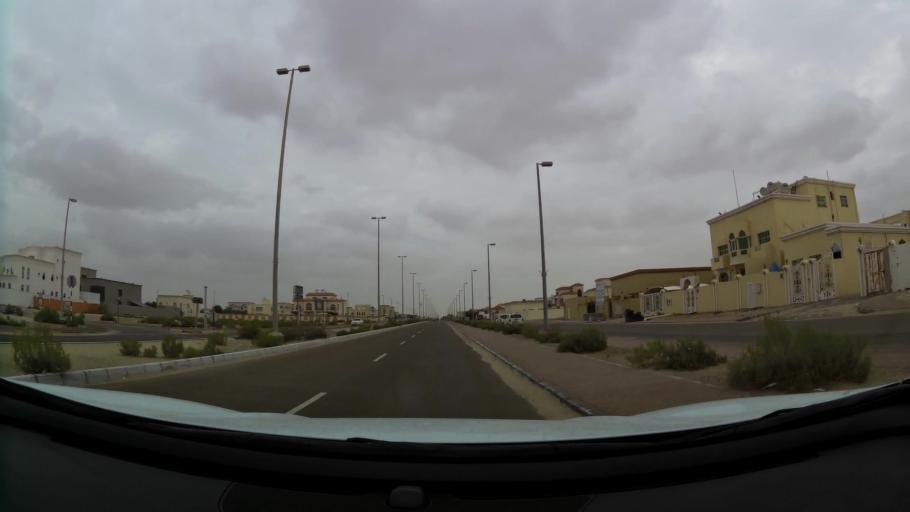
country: AE
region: Abu Dhabi
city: Abu Dhabi
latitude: 24.3772
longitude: 54.6455
